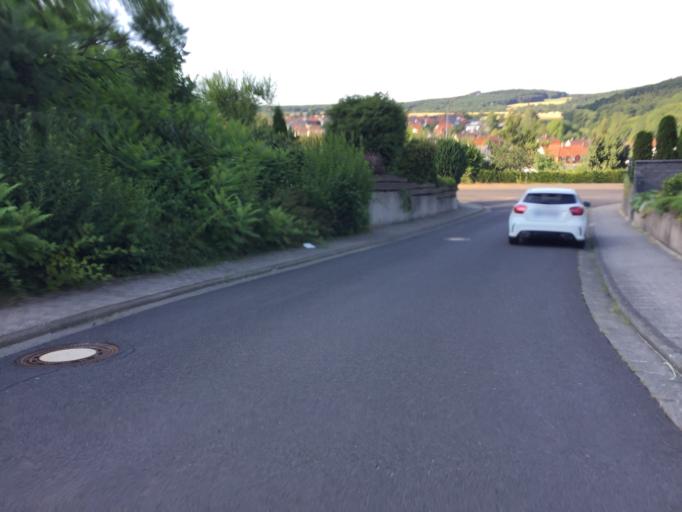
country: DE
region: Hesse
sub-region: Regierungsbezirk Giessen
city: Heuchelheim
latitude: 50.6168
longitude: 8.6397
